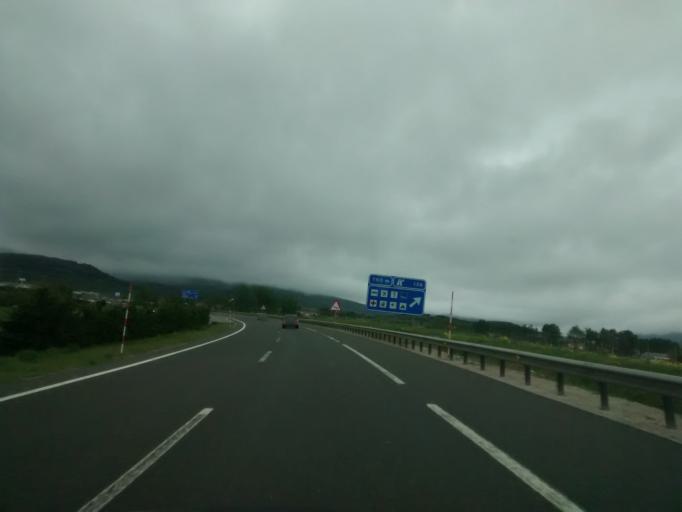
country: ES
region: Cantabria
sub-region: Provincia de Cantabria
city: Reinosa
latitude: 42.9959
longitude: -4.1250
